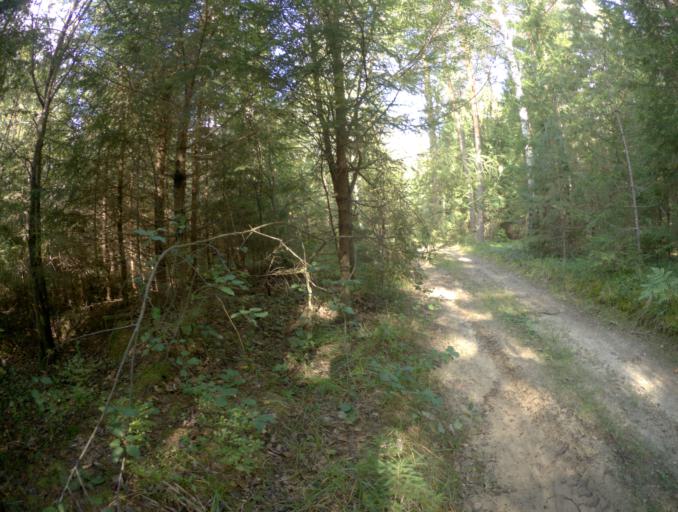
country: RU
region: Vladimir
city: Kommunar
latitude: 56.0308
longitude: 40.5256
